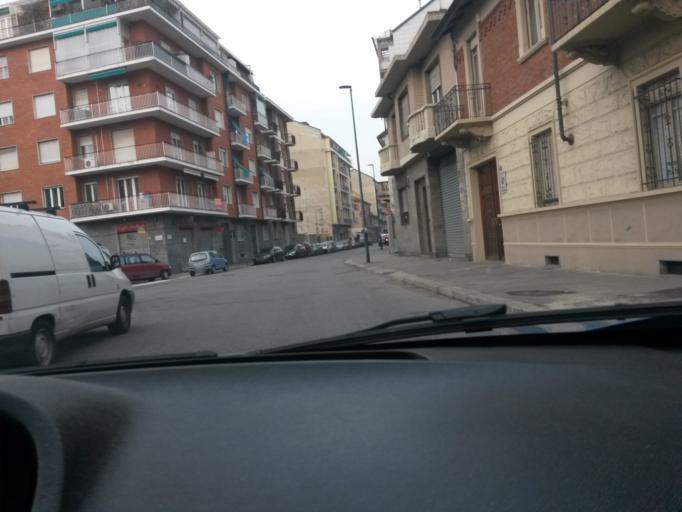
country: IT
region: Piedmont
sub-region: Provincia di Torino
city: Lesna
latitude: 45.0705
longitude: 7.6213
